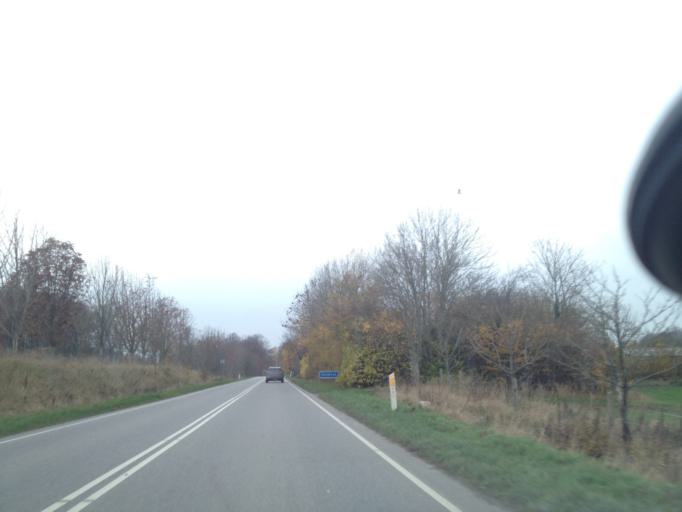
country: DK
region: South Denmark
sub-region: Assens Kommune
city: Vissenbjerg
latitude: 55.4586
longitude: 10.1097
